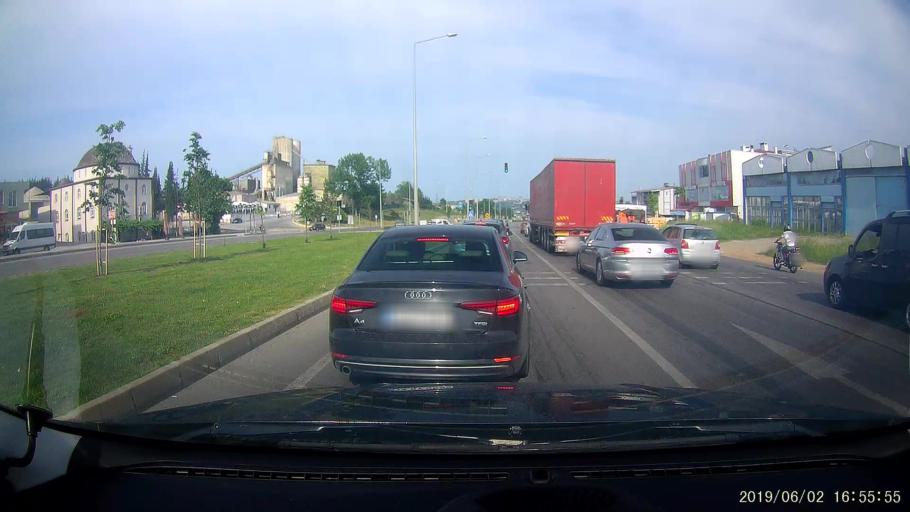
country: TR
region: Samsun
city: Samsun
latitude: 41.2930
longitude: 36.2553
